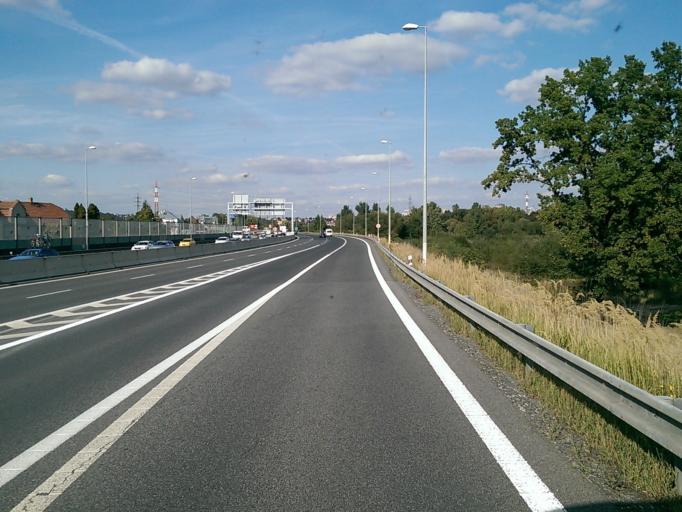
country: CZ
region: Praha
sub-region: Praha 12
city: Modrany
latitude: 49.9876
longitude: 14.3982
